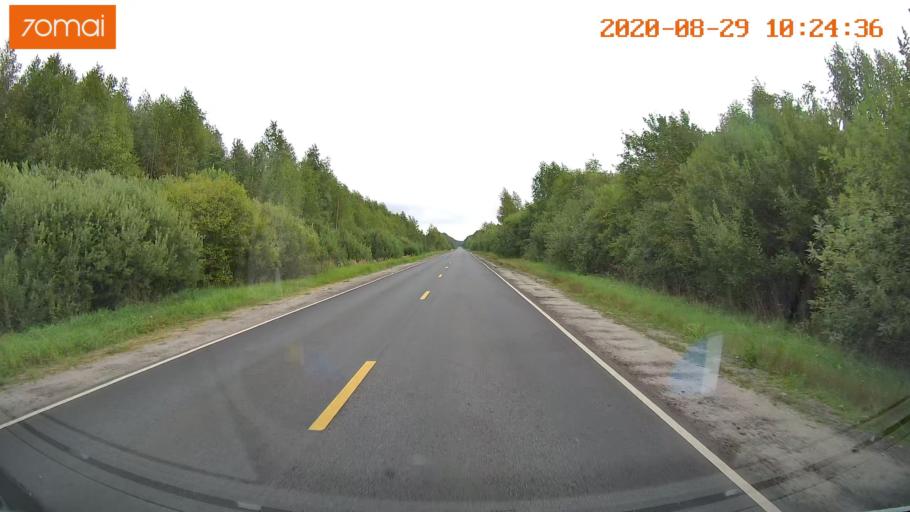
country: RU
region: Ivanovo
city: Yur'yevets
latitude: 57.3208
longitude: 43.0012
